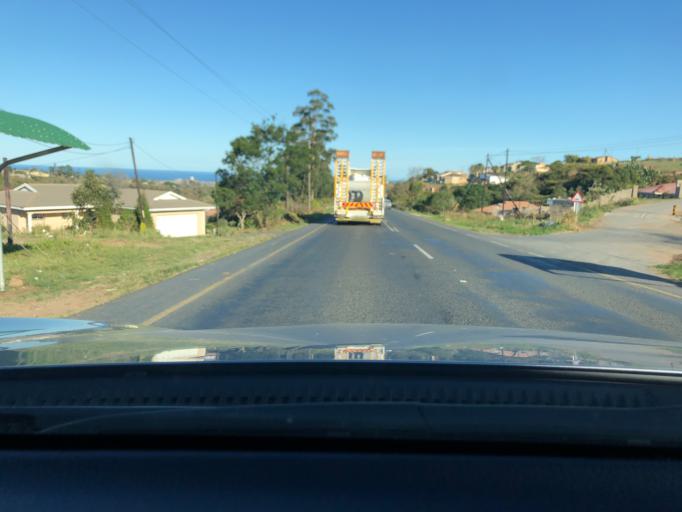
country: ZA
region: KwaZulu-Natal
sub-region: eThekwini Metropolitan Municipality
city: Umkomaas
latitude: -30.0137
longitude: 30.8067
